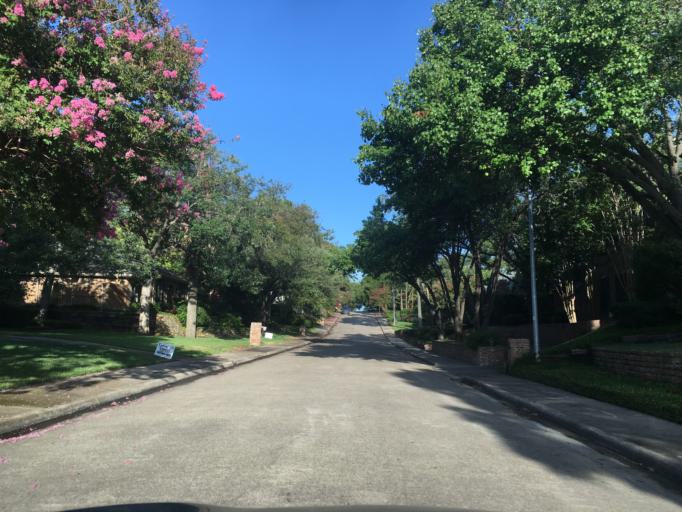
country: US
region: Texas
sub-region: Dallas County
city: Richardson
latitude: 32.8896
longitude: -96.7348
